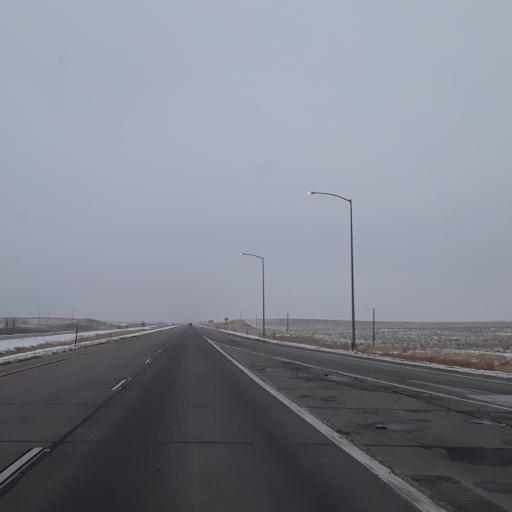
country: US
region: Colorado
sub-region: Logan County
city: Sterling
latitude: 40.5030
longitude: -103.2581
